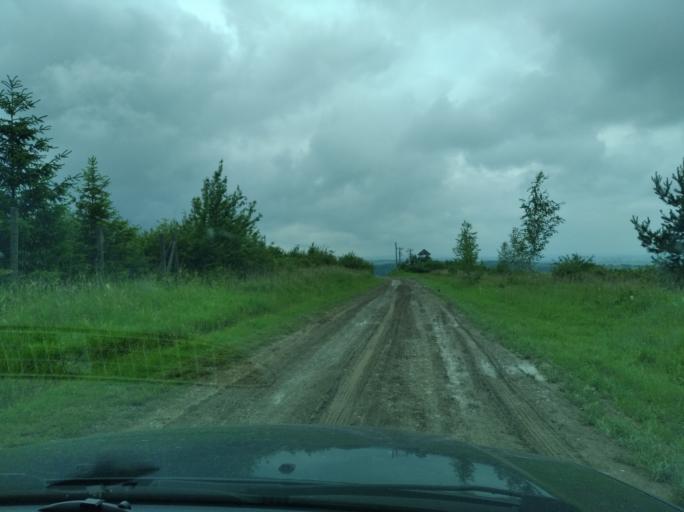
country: PL
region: Subcarpathian Voivodeship
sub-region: Powiat jaroslawski
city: Pruchnik
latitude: 49.8874
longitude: 22.5153
